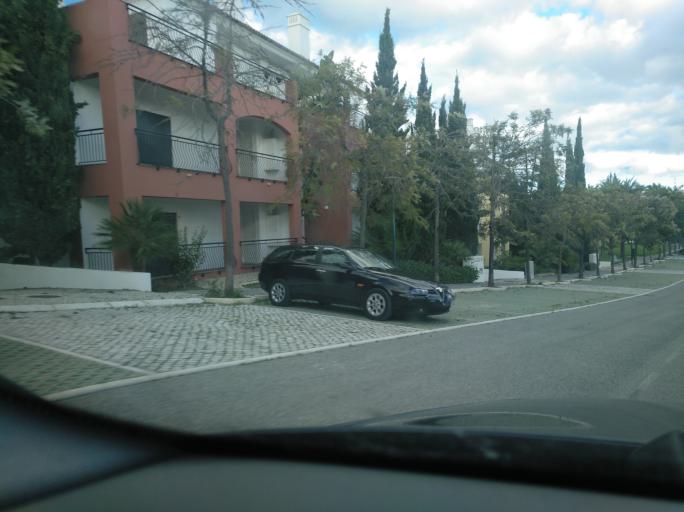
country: PT
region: Faro
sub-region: Tavira
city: Tavira
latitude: 37.1420
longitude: -7.6063
